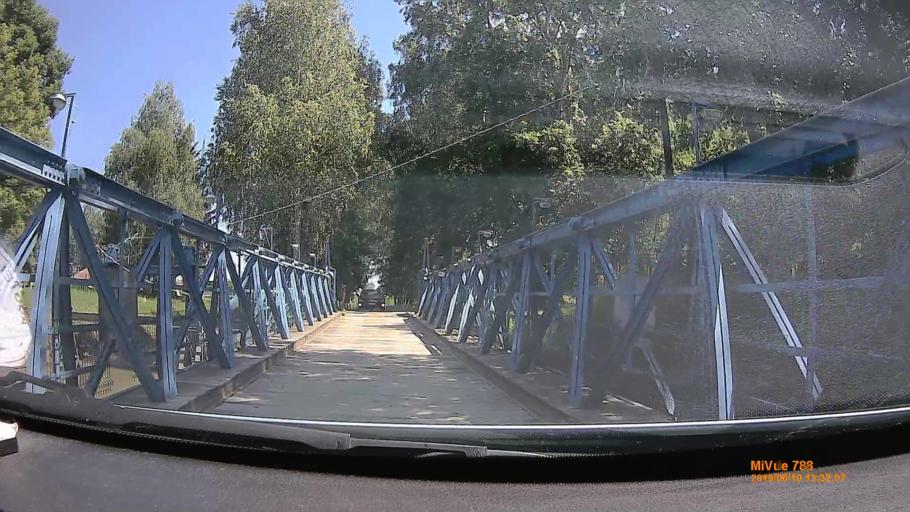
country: HU
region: Szabolcs-Szatmar-Bereg
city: Tiszadob
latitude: 48.0096
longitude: 21.1420
